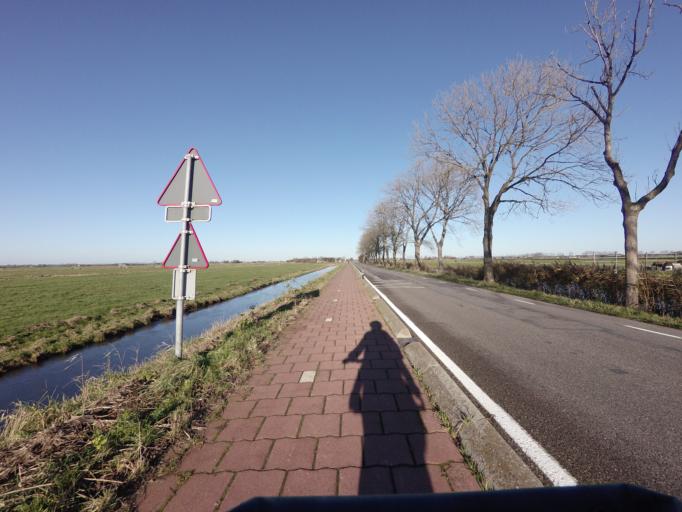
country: NL
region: Utrecht
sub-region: Gemeente De Ronde Venen
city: Mijdrecht
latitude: 52.2237
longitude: 4.9041
